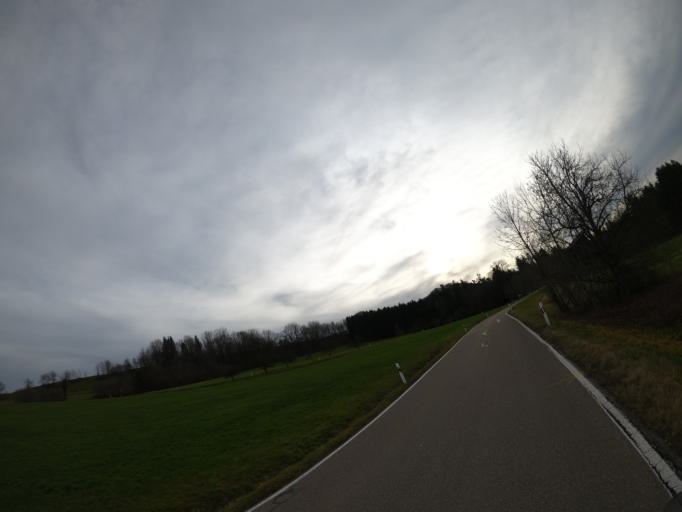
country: DE
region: Baden-Wuerttemberg
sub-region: Regierungsbezirk Stuttgart
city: Ottenbach
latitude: 48.7523
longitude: 9.7221
